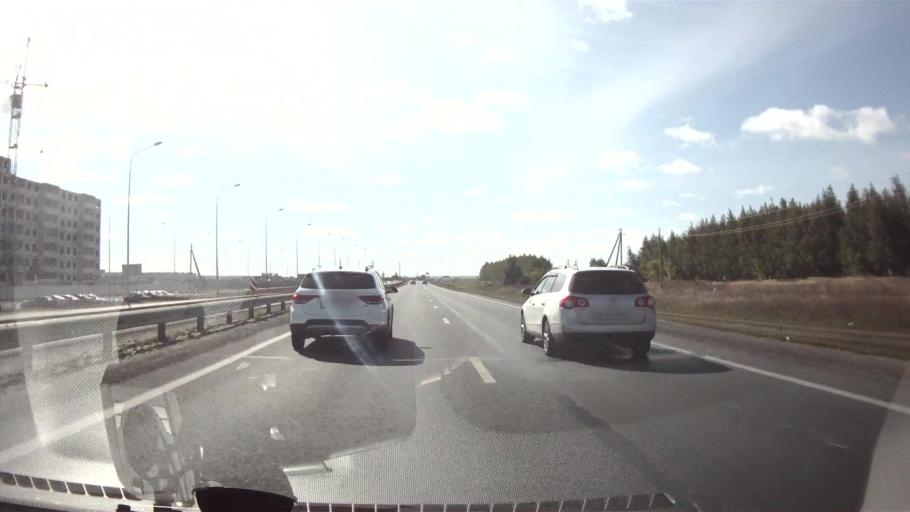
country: RU
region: Ulyanovsk
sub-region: Ulyanovskiy Rayon
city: Ulyanovsk
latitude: 54.2825
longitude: 48.2581
